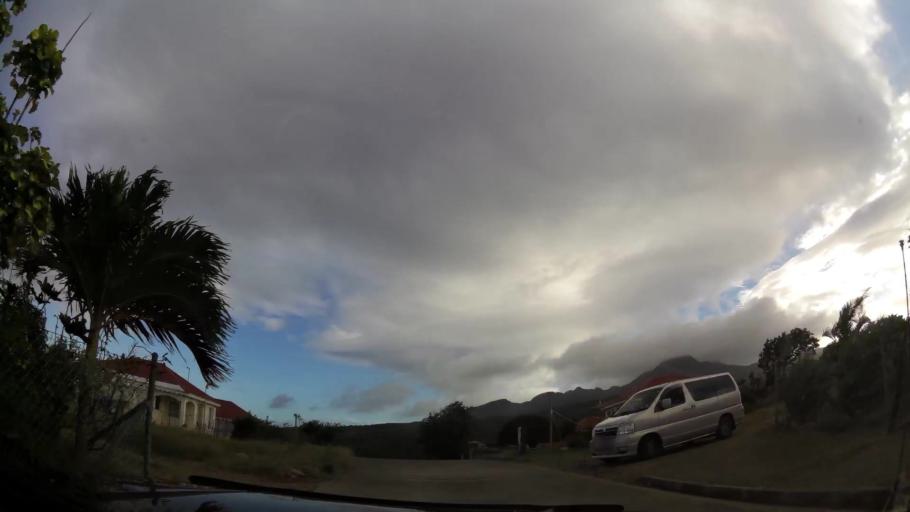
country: MS
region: Saint Peter
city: Brades
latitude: 16.7921
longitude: -62.1867
